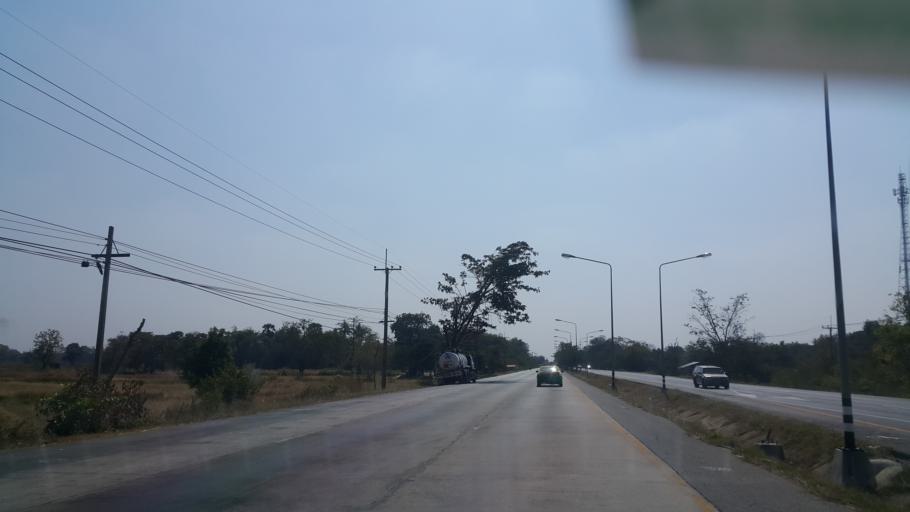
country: TH
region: Nakhon Ratchasima
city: Non Daeng
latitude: 15.4128
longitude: 102.4793
